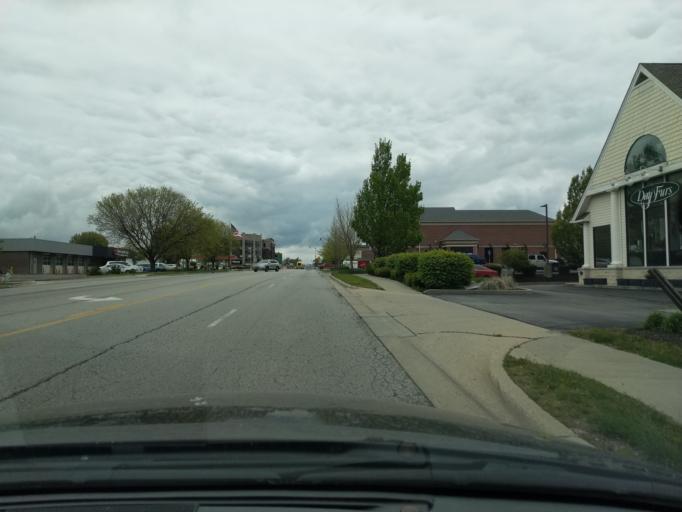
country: US
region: Indiana
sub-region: Hamilton County
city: Carmel
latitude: 39.9591
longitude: -86.1267
